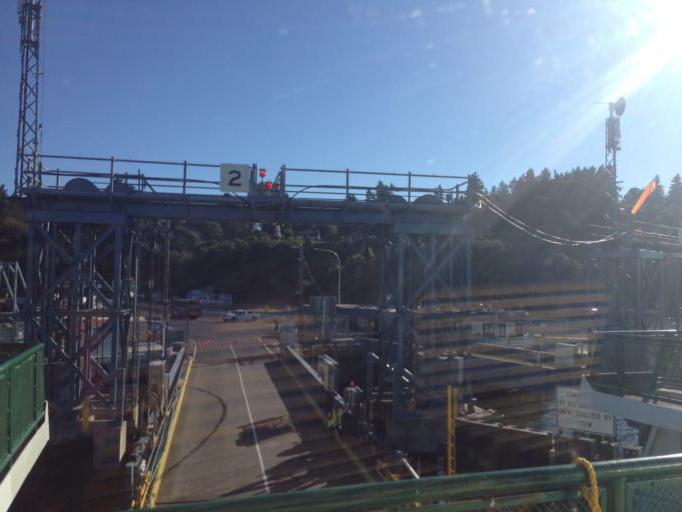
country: US
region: Washington
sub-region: Kitsap County
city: Southworth
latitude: 47.5109
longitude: -122.4633
